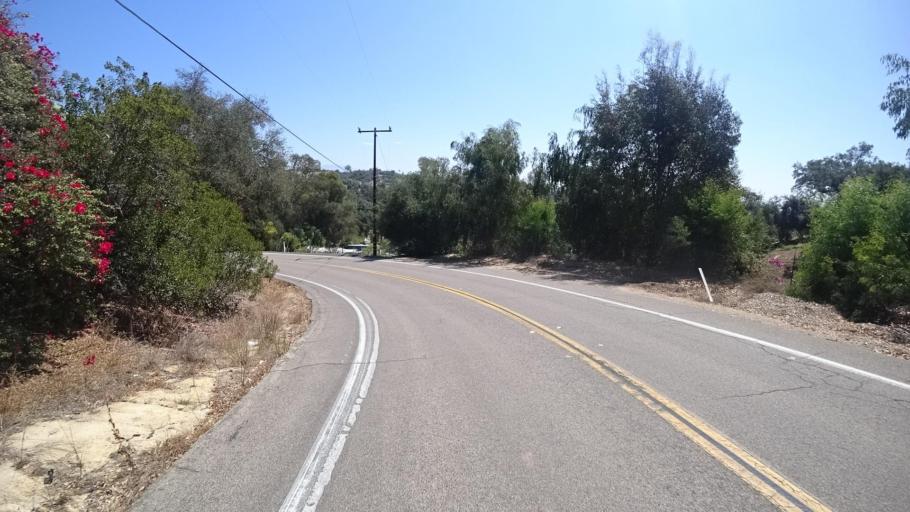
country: US
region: California
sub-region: San Diego County
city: Fallbrook
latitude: 33.3801
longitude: -117.2121
